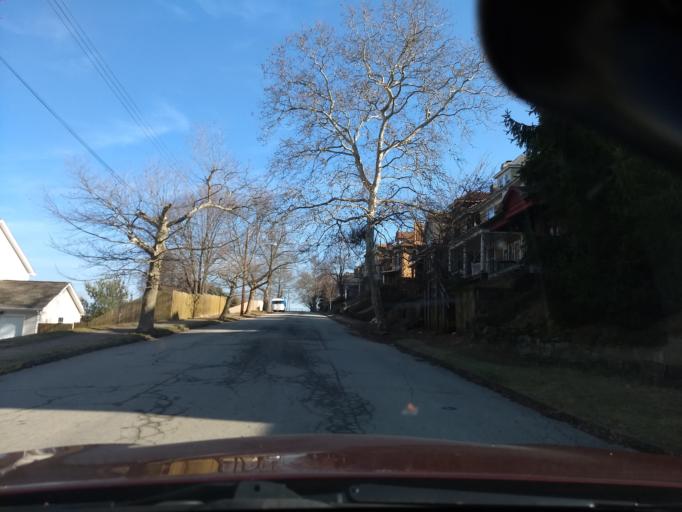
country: US
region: Pennsylvania
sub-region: Allegheny County
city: Homestead
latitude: 40.4059
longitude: -79.9025
